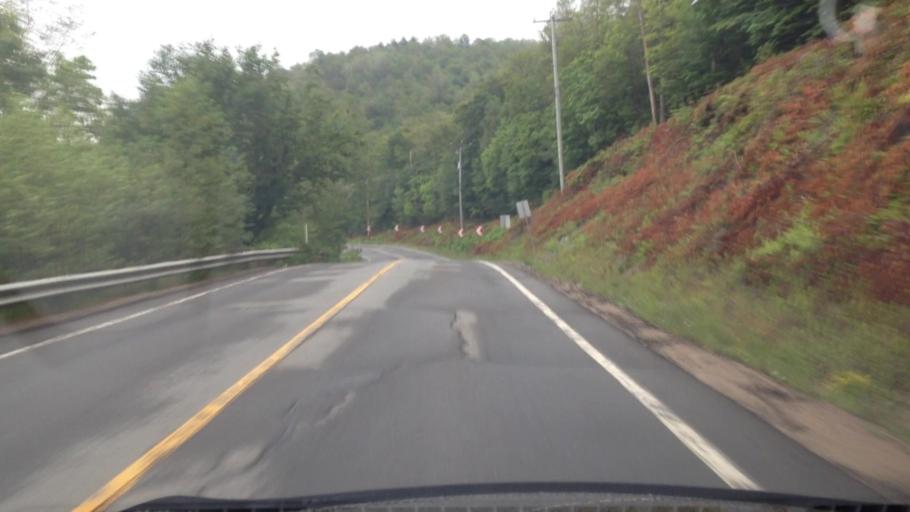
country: CA
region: Quebec
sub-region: Laurentides
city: Sainte-Agathe-des-Monts
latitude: 45.9225
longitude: -74.4887
